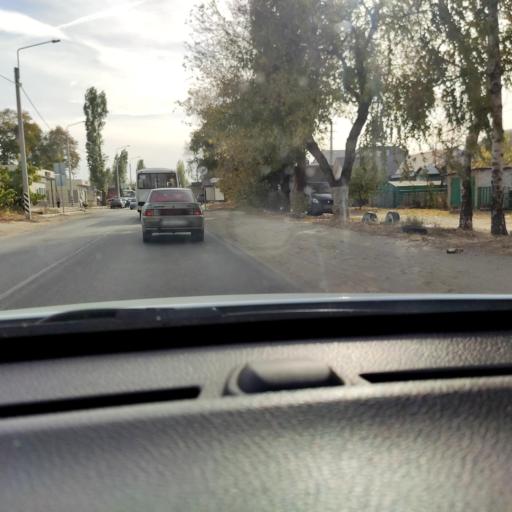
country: RU
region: Voronezj
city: Maslovka
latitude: 51.5511
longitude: 39.2352
